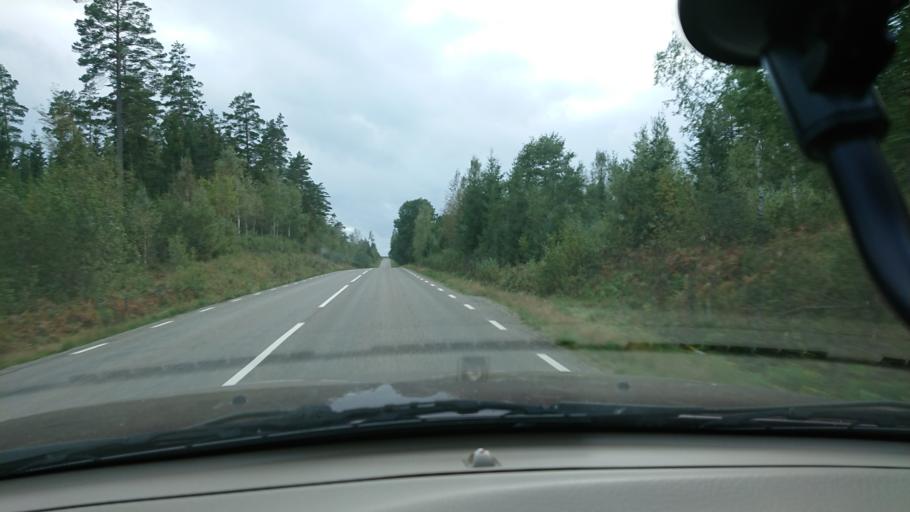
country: SE
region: Kronoberg
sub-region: Vaxjo Kommun
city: Lammhult
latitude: 57.0956
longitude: 14.6735
